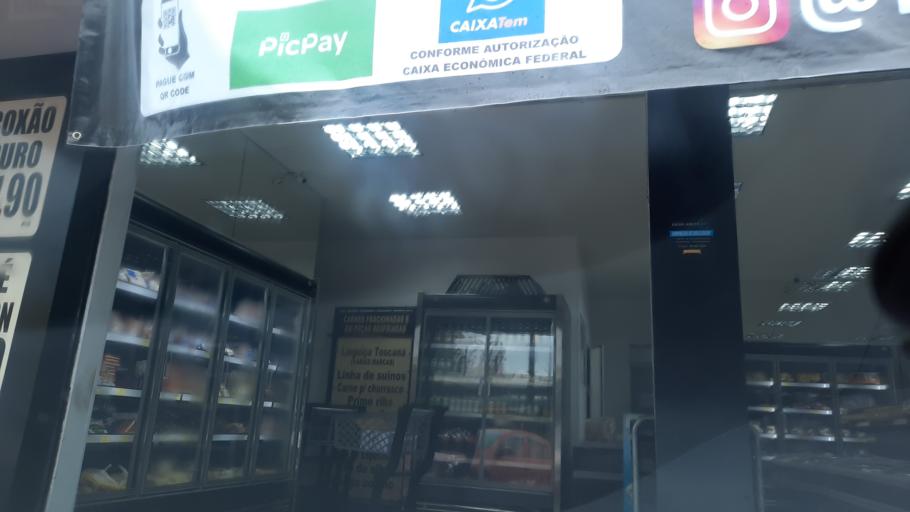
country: BR
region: Sao Paulo
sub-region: Guarulhos
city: Guarulhos
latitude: -23.4594
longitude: -46.5647
